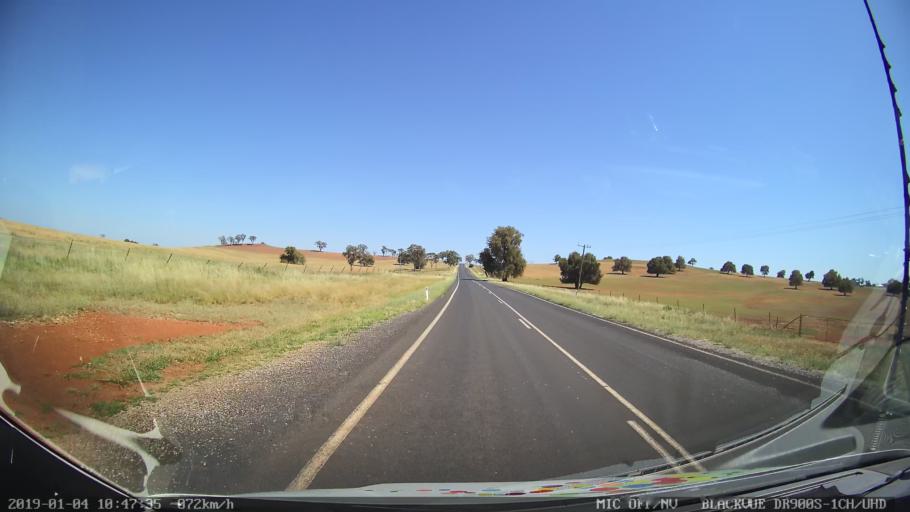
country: AU
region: New South Wales
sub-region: Cabonne
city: Molong
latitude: -33.2685
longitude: 148.7188
